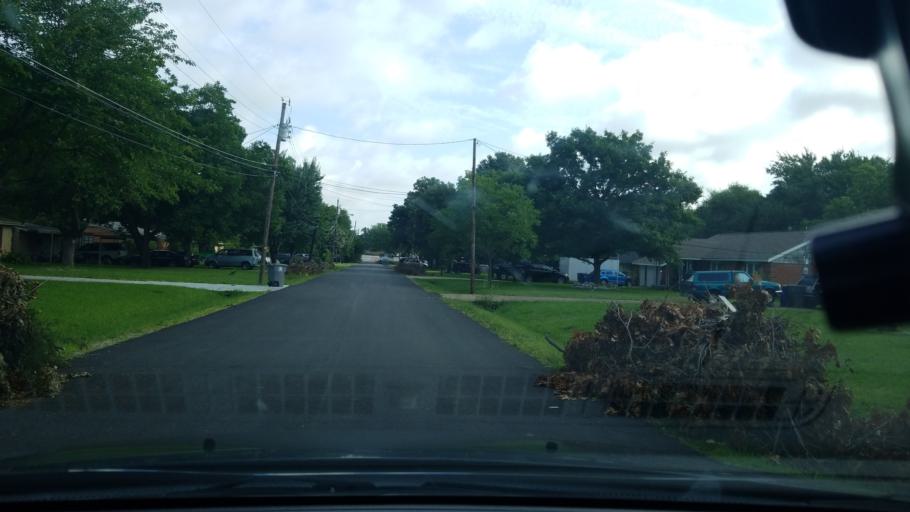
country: US
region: Texas
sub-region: Dallas County
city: Mesquite
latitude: 32.8193
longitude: -96.6637
